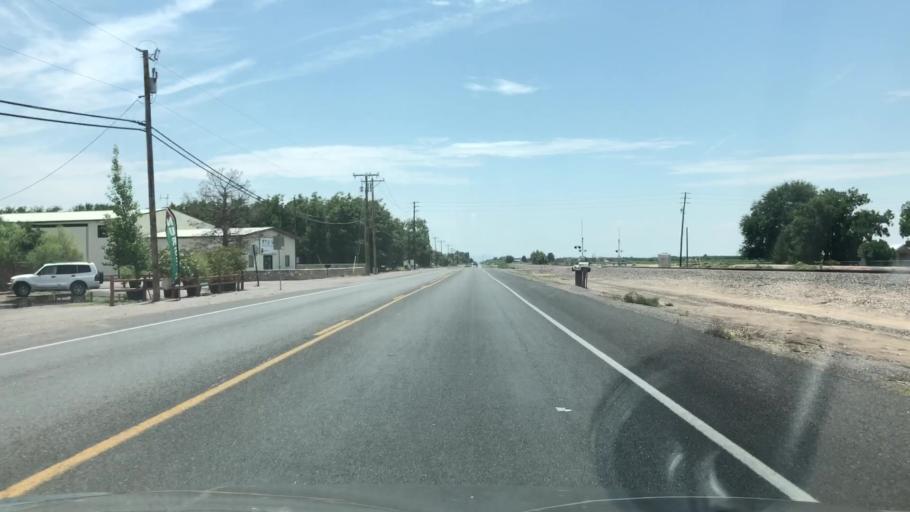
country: US
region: New Mexico
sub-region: Dona Ana County
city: University Park
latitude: 32.2496
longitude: -106.7503
